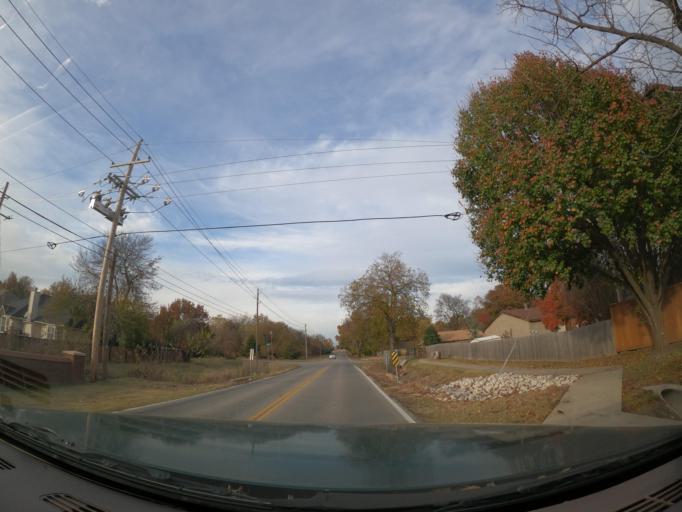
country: US
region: Oklahoma
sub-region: Tulsa County
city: Jenks
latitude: 36.0391
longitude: -95.9400
